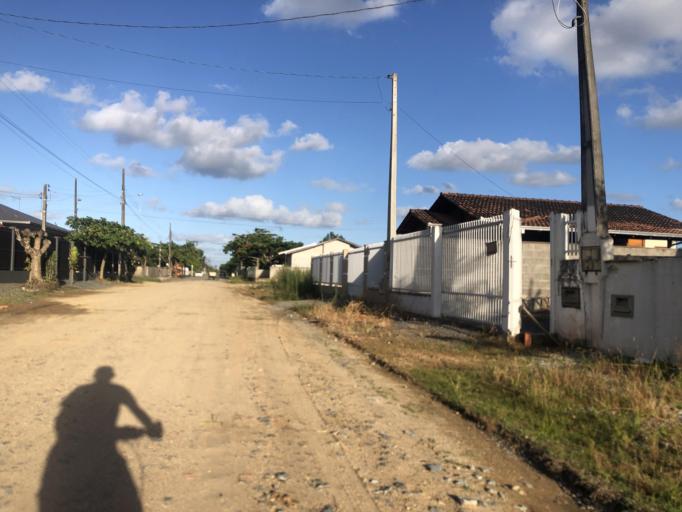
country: BR
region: Santa Catarina
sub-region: Sao Francisco Do Sul
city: Sao Francisco do Sul
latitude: -26.2183
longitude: -48.5327
